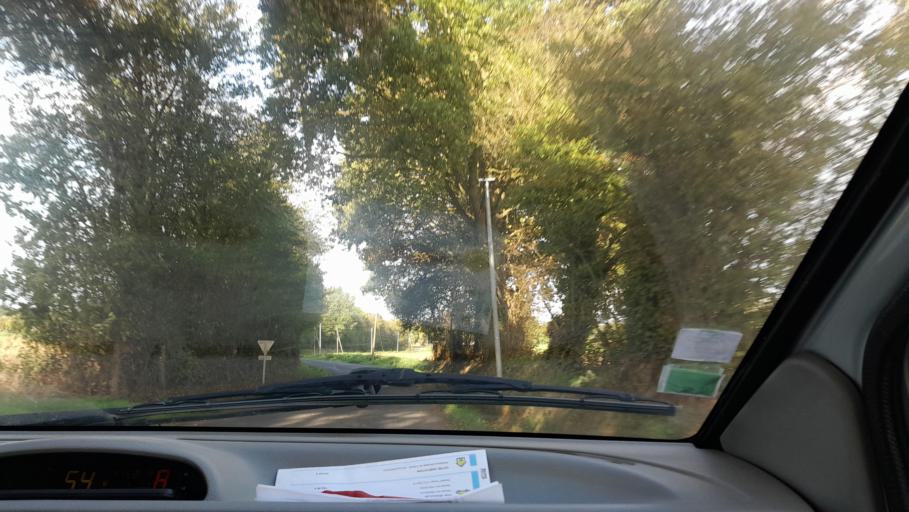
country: FR
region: Lower Normandy
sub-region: Departement de la Manche
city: Pontorson
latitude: 48.5564
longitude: -1.4570
